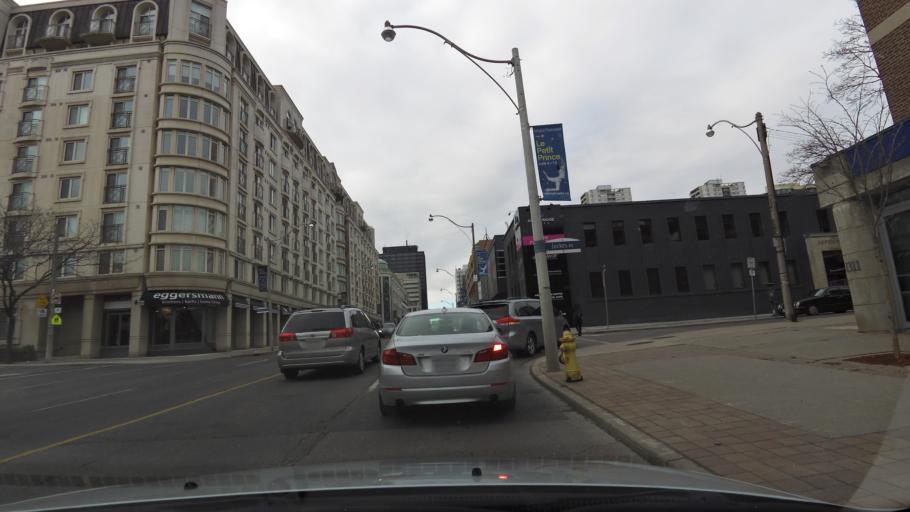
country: CA
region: Ontario
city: Toronto
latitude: 43.6851
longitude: -79.3927
